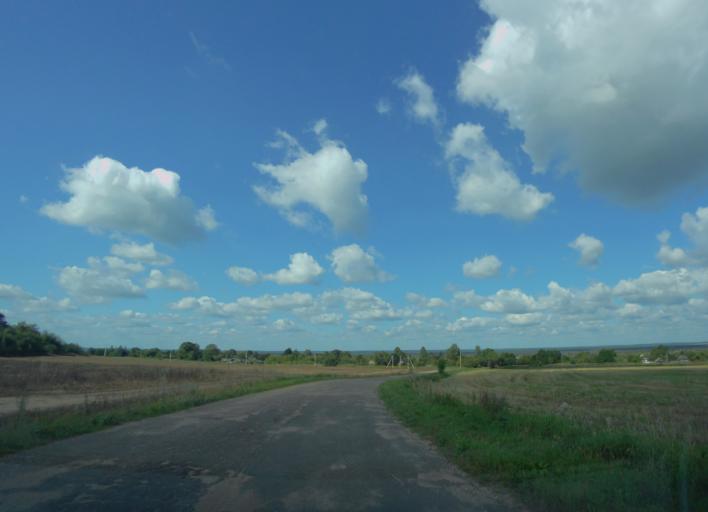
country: BY
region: Minsk
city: Zyembin
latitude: 54.4071
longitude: 28.3902
